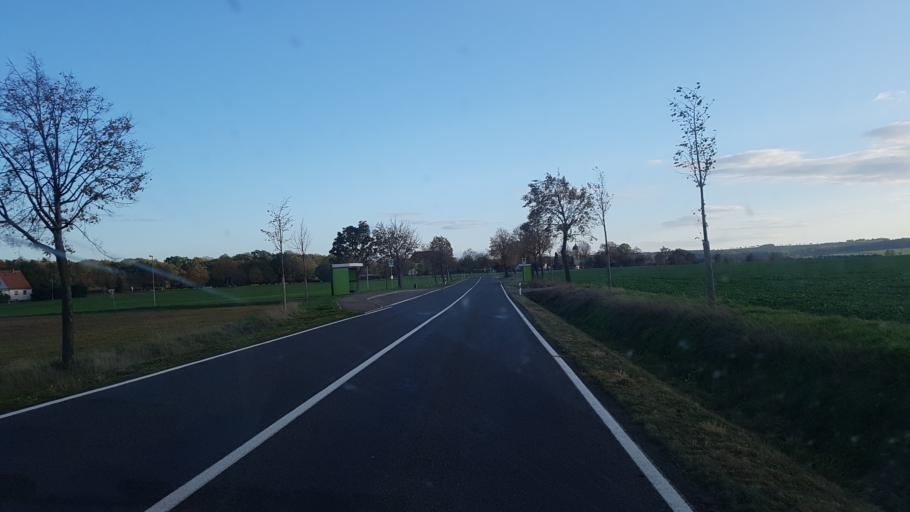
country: DE
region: Saxony
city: Dahlen
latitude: 51.3447
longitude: 13.0295
